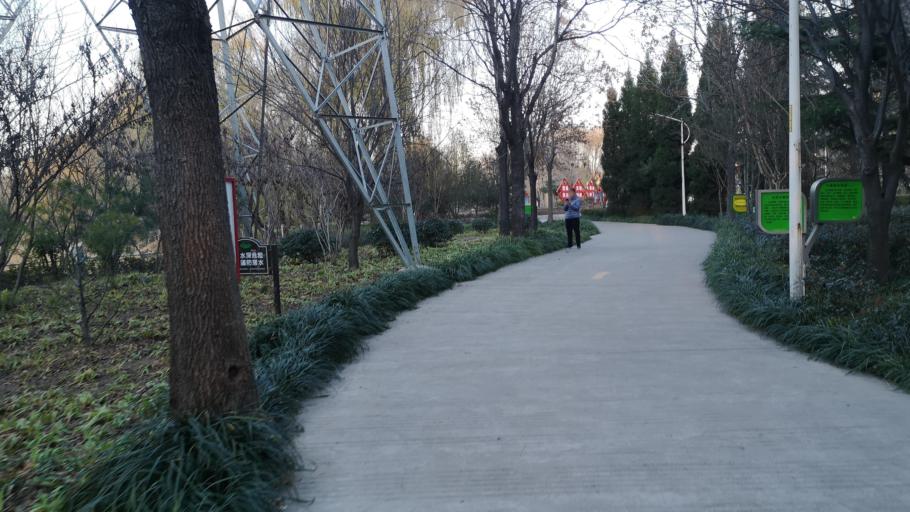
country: CN
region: Henan Sheng
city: Puyang
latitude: 35.7627
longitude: 115.0018
